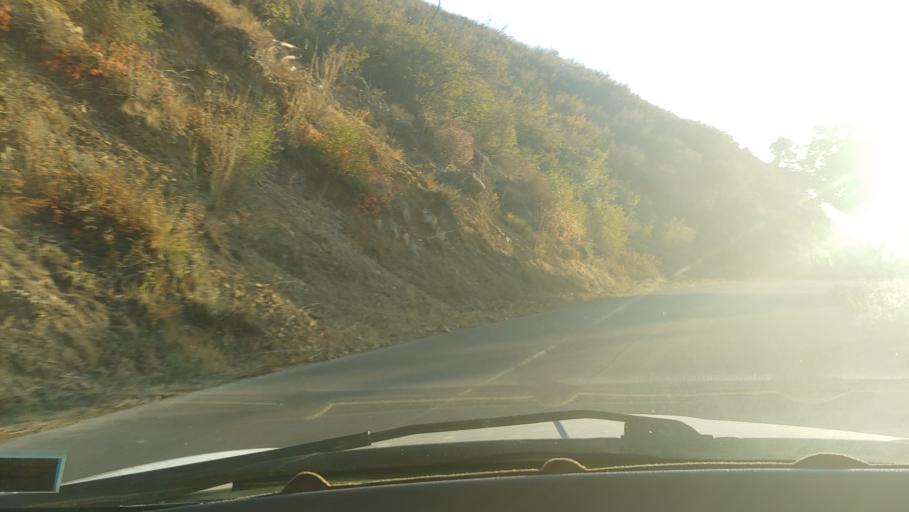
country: US
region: California
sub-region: Santa Barbara County
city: Mission Canyon
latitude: 34.4752
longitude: -119.6790
